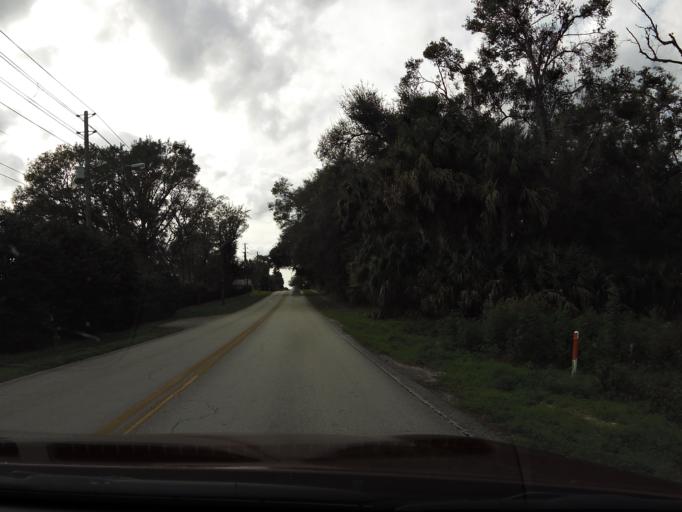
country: US
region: Florida
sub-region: Volusia County
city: Orange City
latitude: 28.9487
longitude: -81.2833
